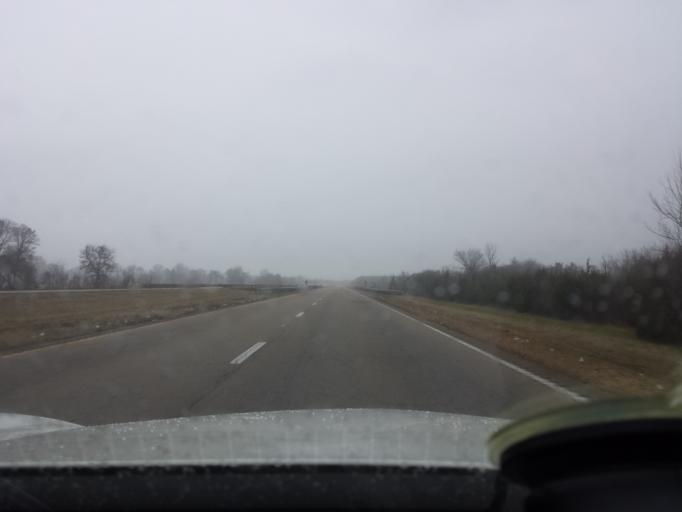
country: US
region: Mississippi
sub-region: Lee County
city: Shannon
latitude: 34.0547
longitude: -88.7025
